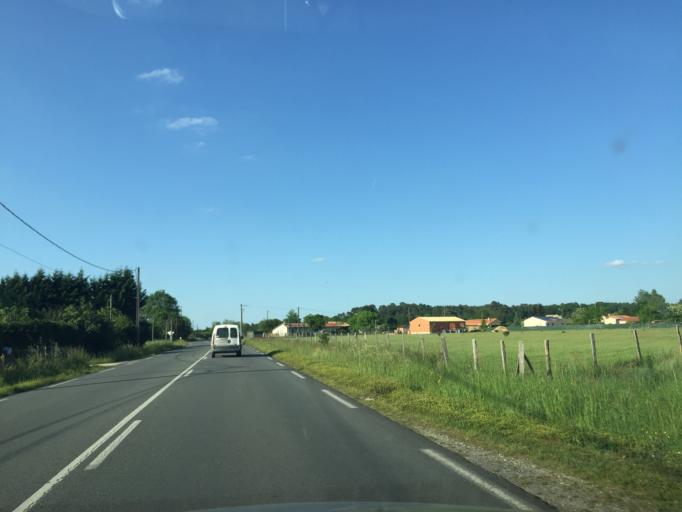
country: FR
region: Poitou-Charentes
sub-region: Departement de la Charente-Maritime
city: Saint-Aigulin
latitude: 45.1322
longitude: -0.0055
